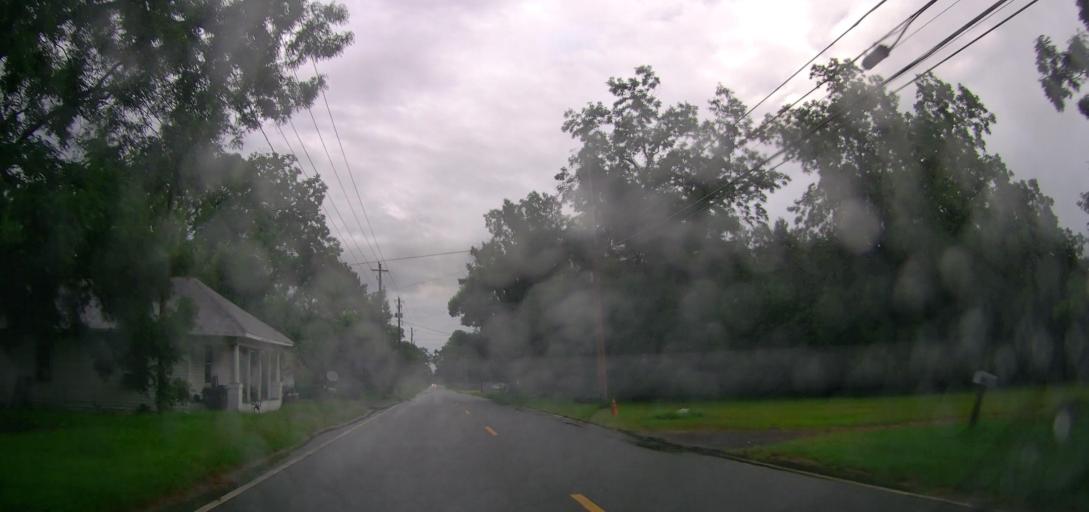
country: US
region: Georgia
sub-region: Ware County
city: Waycross
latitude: 31.1985
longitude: -82.3752
